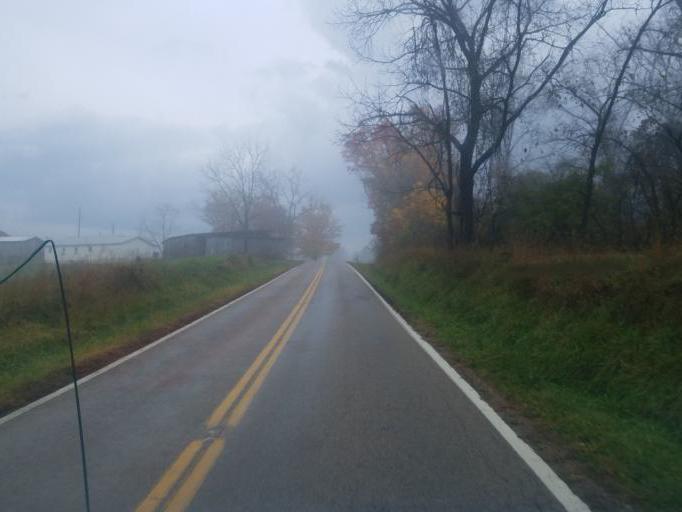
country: US
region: Ohio
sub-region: Morgan County
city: McConnelsville
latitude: 39.5111
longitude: -81.9107
